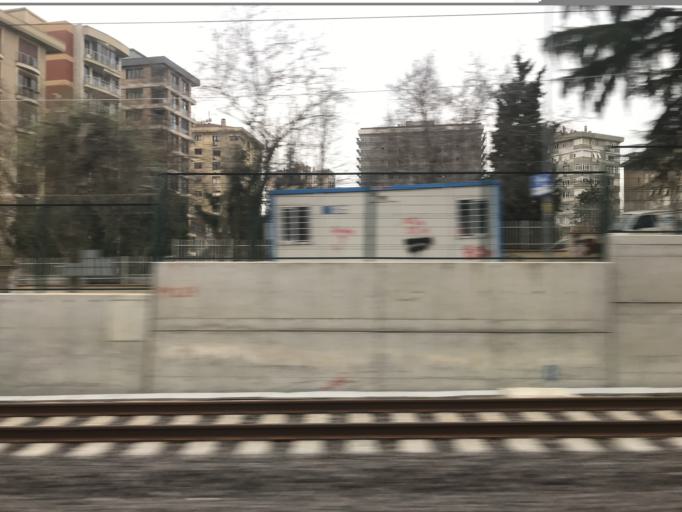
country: TR
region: Istanbul
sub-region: Atasehir
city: Atasehir
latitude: 40.9583
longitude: 29.0892
